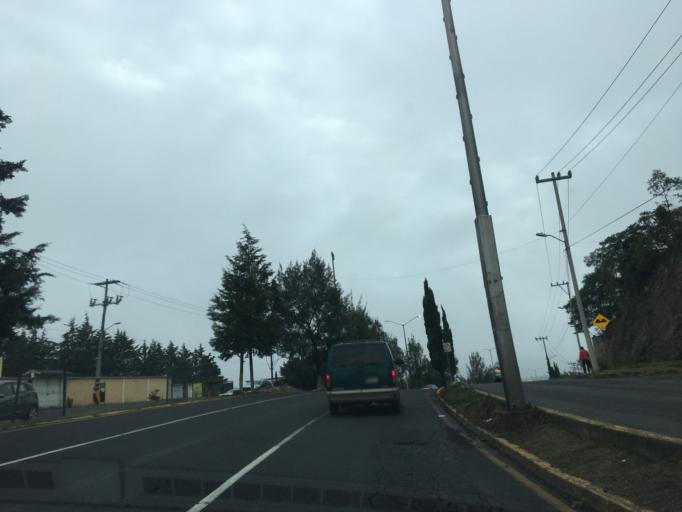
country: MX
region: Mexico
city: Ciudad Lopez Mateos
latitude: 19.5553
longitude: -99.2960
